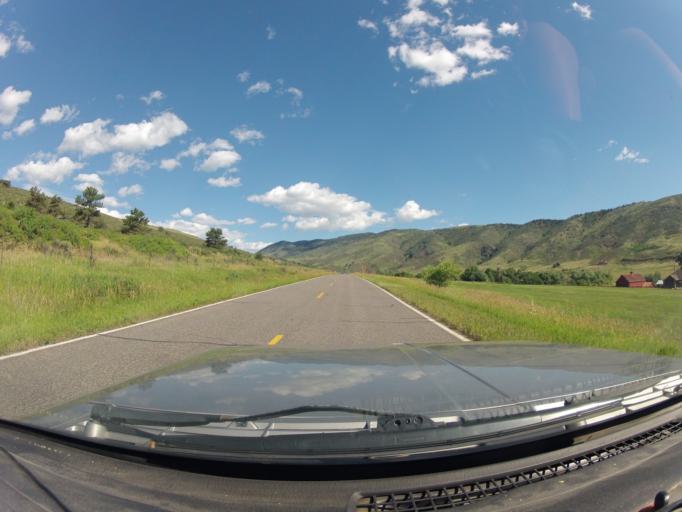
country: US
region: Colorado
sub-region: Larimer County
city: Laporte
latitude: 40.4972
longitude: -105.2239
